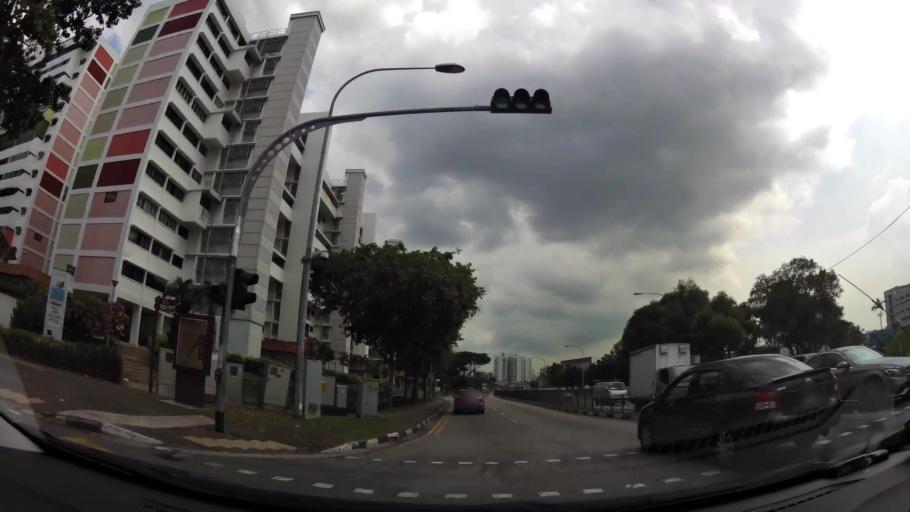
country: SG
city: Singapore
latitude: 1.3183
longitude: 103.7478
